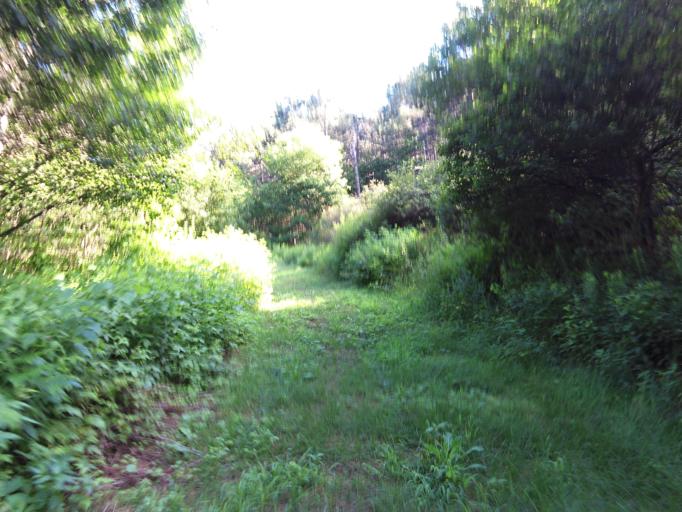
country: CA
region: Ontario
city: Bells Corners
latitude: 45.3169
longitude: -75.7389
